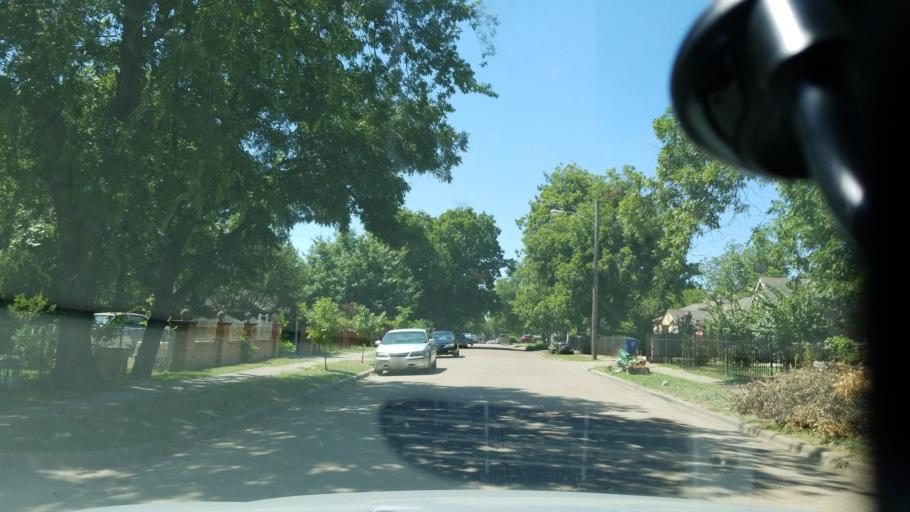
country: US
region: Texas
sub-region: Dallas County
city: Cockrell Hill
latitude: 32.7086
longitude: -96.8171
